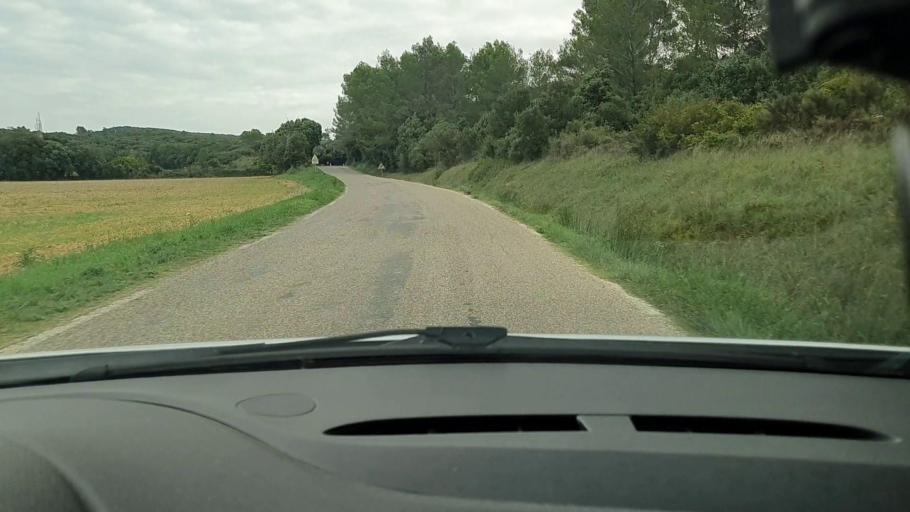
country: FR
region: Languedoc-Roussillon
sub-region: Departement du Gard
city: Montaren-et-Saint-Mediers
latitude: 44.0488
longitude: 4.3145
